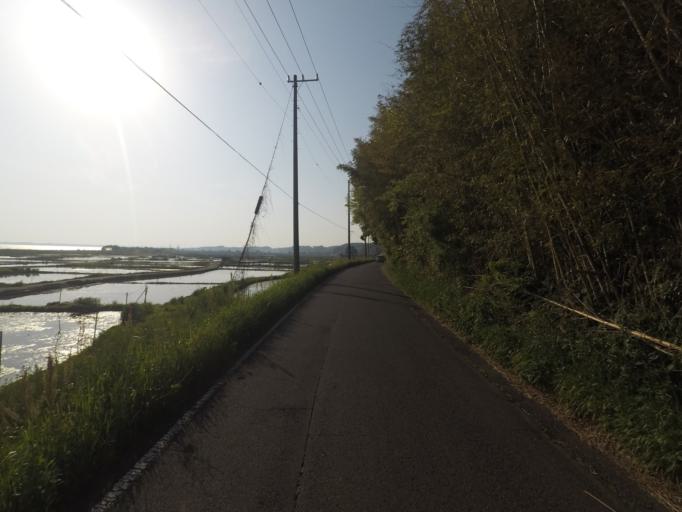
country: JP
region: Ibaraki
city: Ami
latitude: 36.0649
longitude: 140.2879
